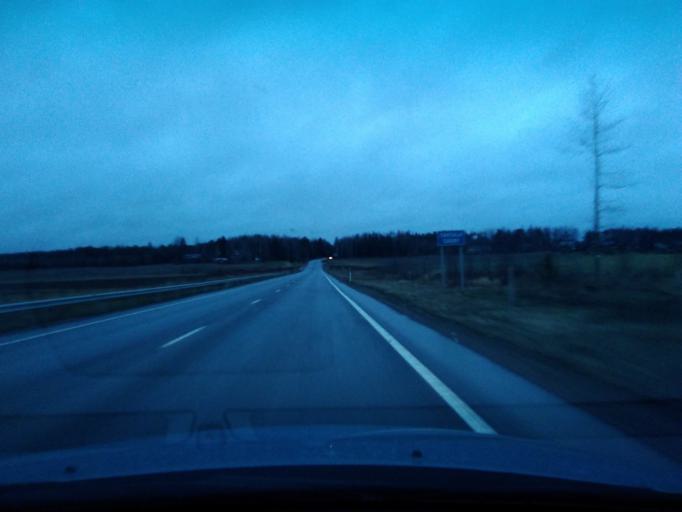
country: FI
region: Uusimaa
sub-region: Porvoo
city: Porvoo
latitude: 60.4133
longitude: 25.5814
